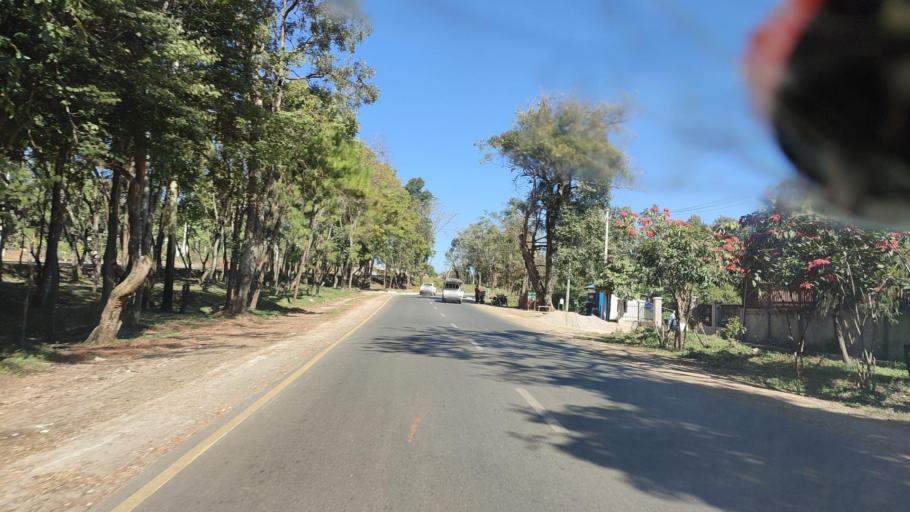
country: MM
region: Mandalay
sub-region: Pyin Oo Lwin District
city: Pyin Oo Lwin
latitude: 21.9976
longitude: 96.4302
